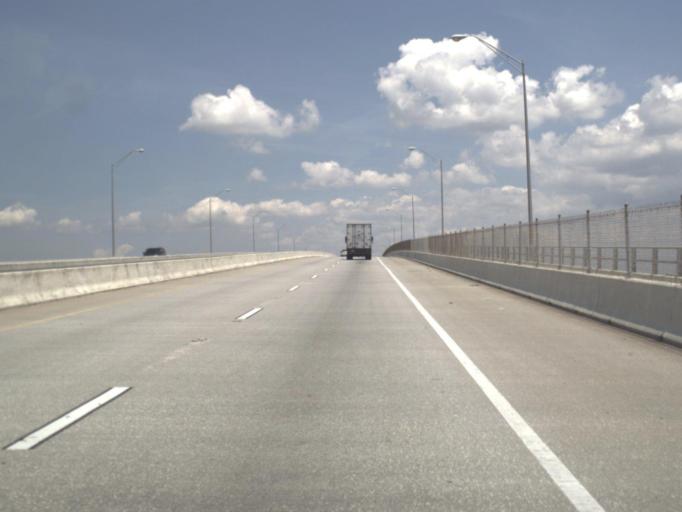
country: US
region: Florida
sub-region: Pinellas County
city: Tierra Verde
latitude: 27.6895
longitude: -82.6786
